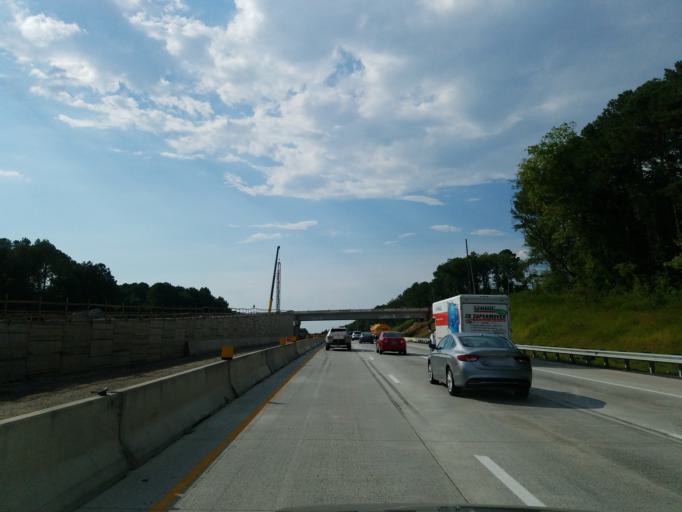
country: US
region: Georgia
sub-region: Cobb County
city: Kennesaw
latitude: 34.0632
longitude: -84.6069
